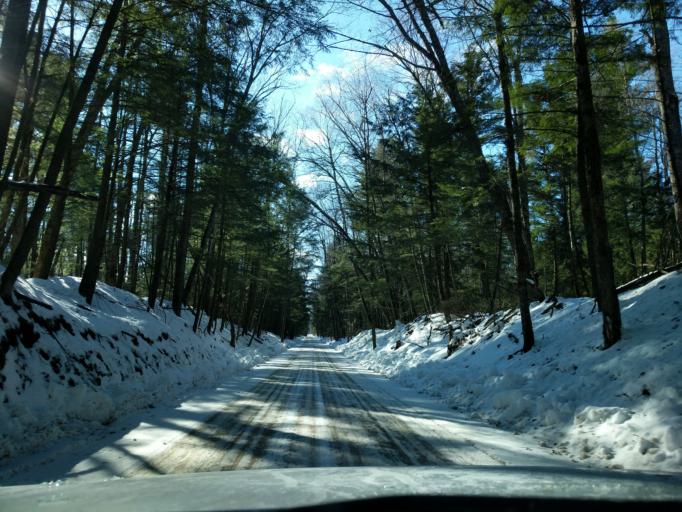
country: US
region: Wisconsin
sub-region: Menominee County
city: Keshena
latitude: 45.0923
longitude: -88.6200
